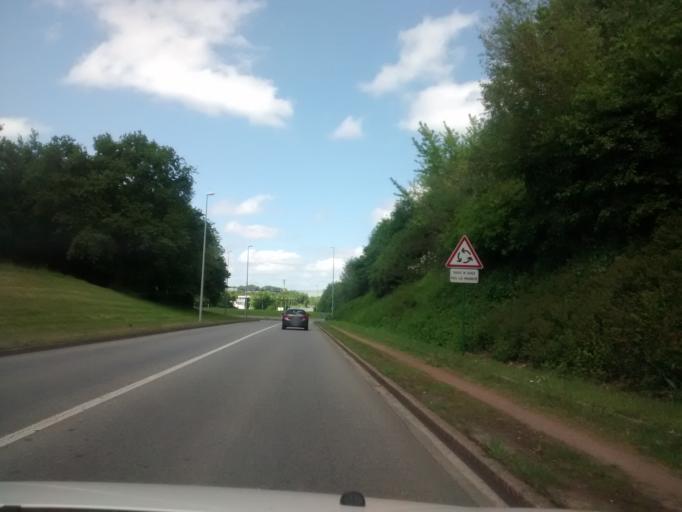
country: FR
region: Brittany
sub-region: Departement d'Ille-et-Vilaine
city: Cesson-Sevigne
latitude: 48.1255
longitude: -1.6209
